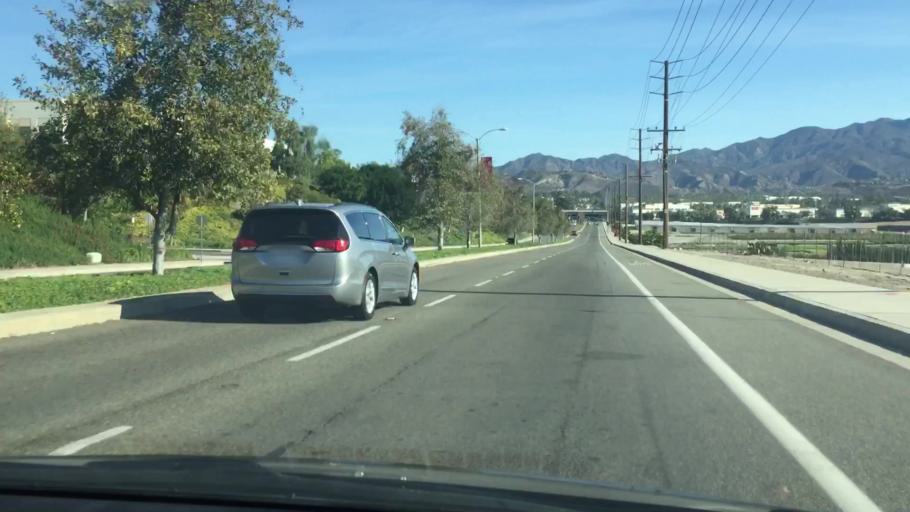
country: US
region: California
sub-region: Orange County
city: Foothill Ranch
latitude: 33.6689
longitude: -117.6724
